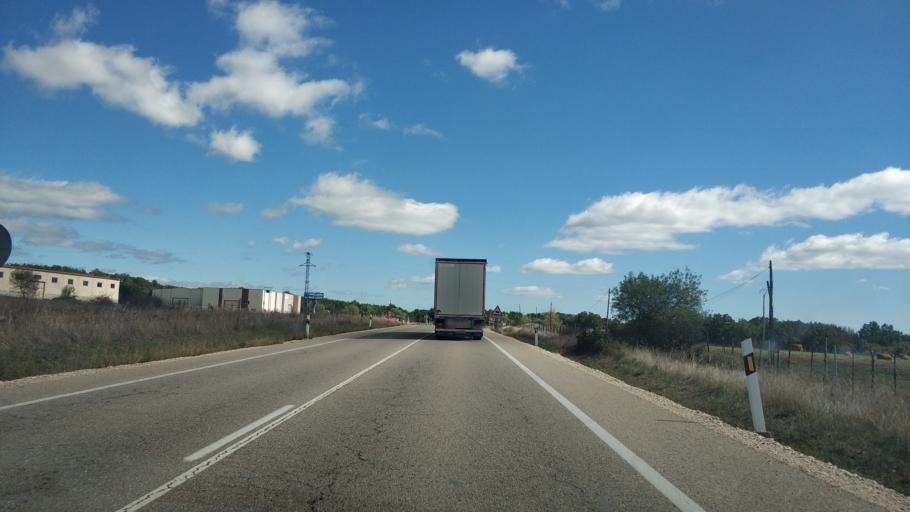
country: ES
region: Castille and Leon
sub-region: Provincia de Burgos
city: Barbadillo del Mercado
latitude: 42.0261
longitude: -3.3271
